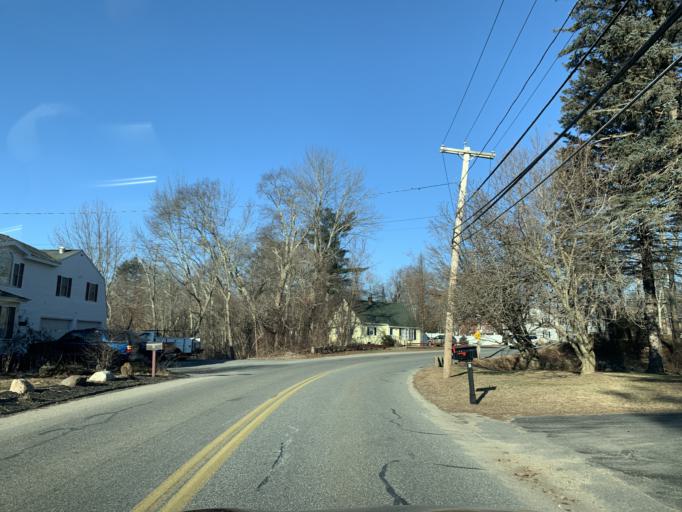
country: US
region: Massachusetts
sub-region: Essex County
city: Methuen
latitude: 42.7072
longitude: -71.2258
